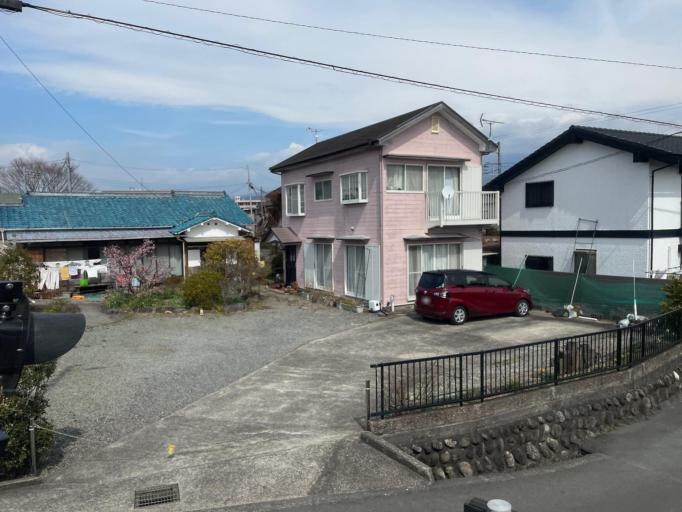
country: JP
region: Shizuoka
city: Fujinomiya
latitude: 35.2157
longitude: 138.6219
